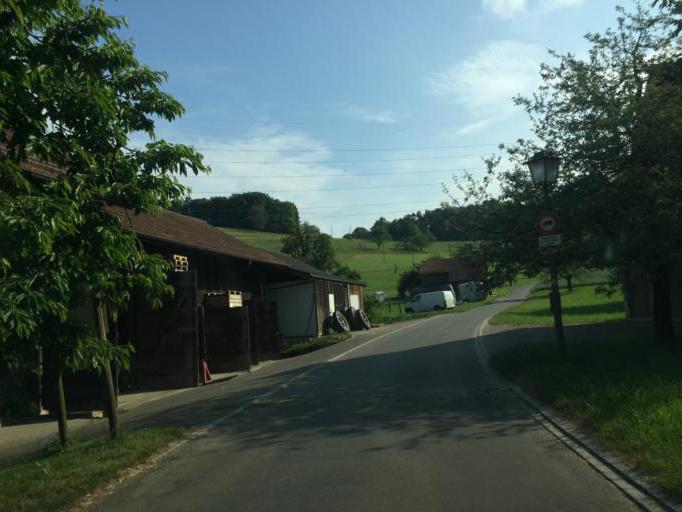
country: CH
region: Zurich
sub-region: Bezirk Buelach
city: Buelach / Gstueckt
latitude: 47.5313
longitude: 8.5567
